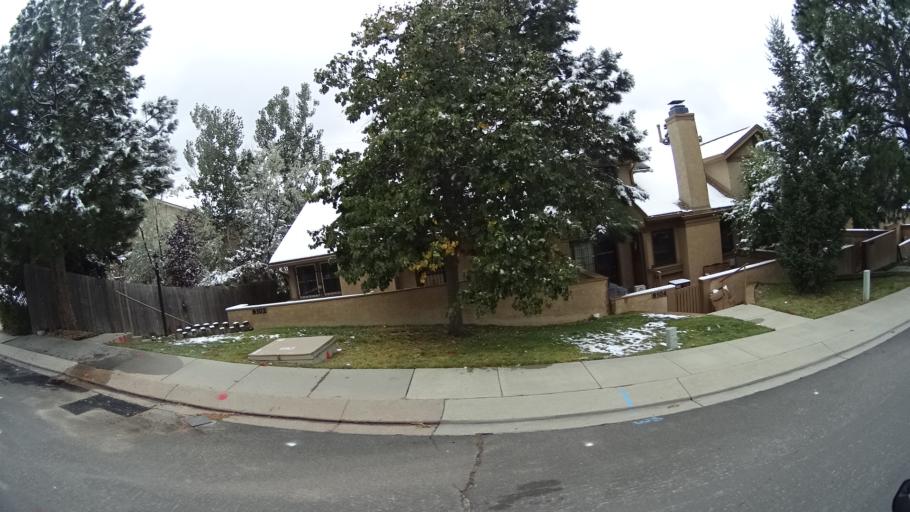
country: US
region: Colorado
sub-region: El Paso County
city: Colorado Springs
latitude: 38.9198
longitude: -104.7932
